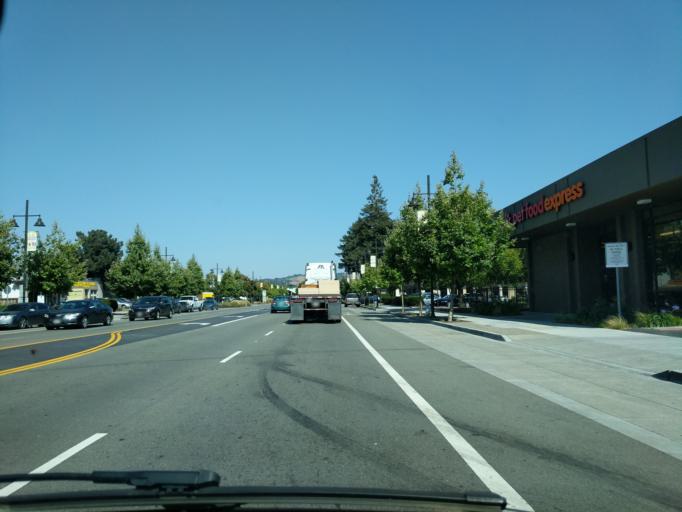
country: US
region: California
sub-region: Alameda County
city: Castro Valley
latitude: 37.6955
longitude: -122.0767
